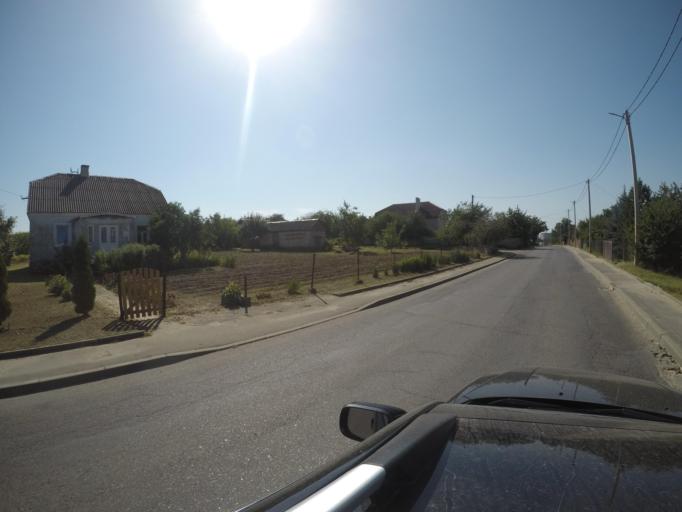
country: BY
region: Grodnenskaya
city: Hrodna
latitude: 53.7086
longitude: 23.8666
